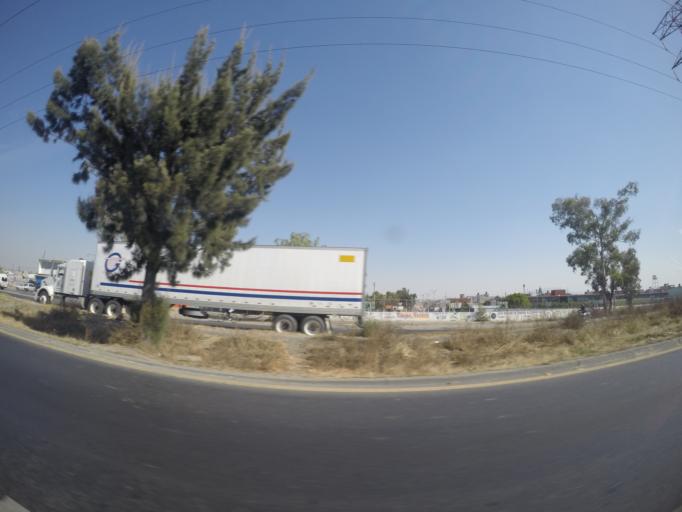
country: MX
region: Mexico
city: Santo Tomas Chiconautla
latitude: 19.6150
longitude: -99.0182
